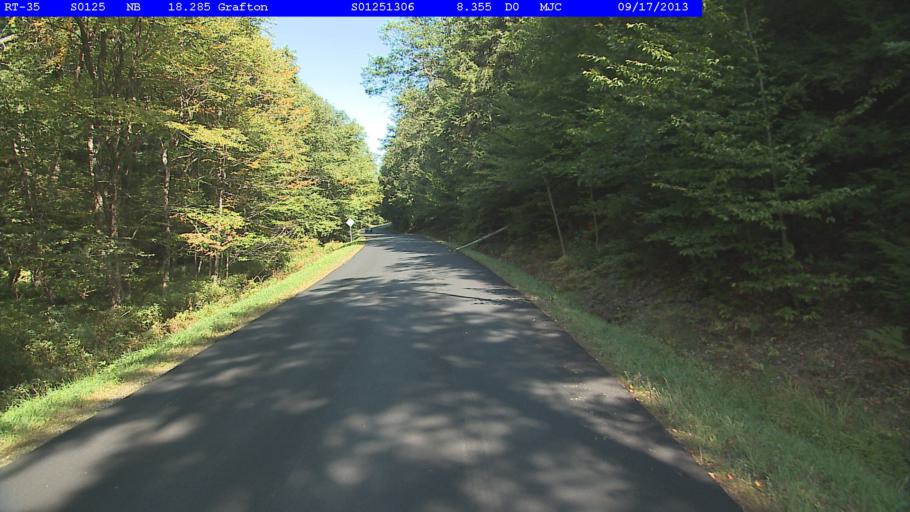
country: US
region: Vermont
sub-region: Windsor County
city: Chester
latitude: 43.2262
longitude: -72.6046
